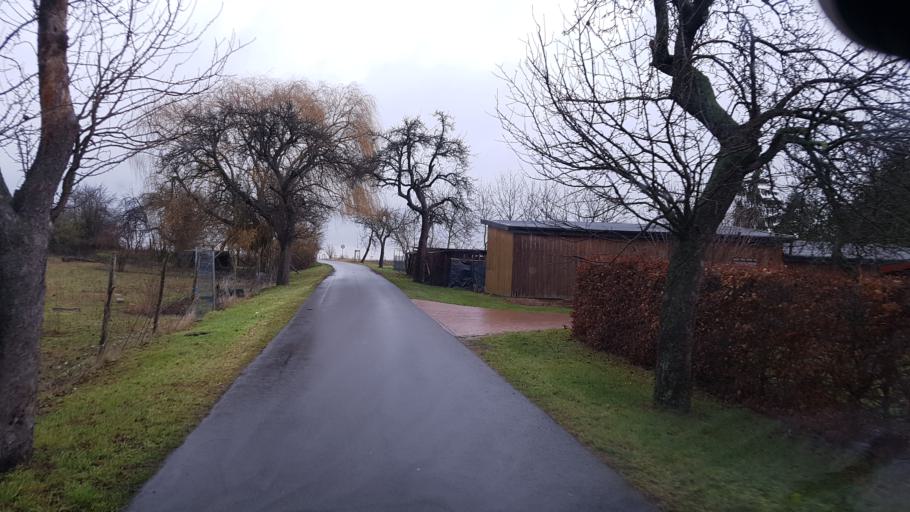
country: DE
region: Brandenburg
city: Altdobern
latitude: 51.6757
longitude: 13.9866
